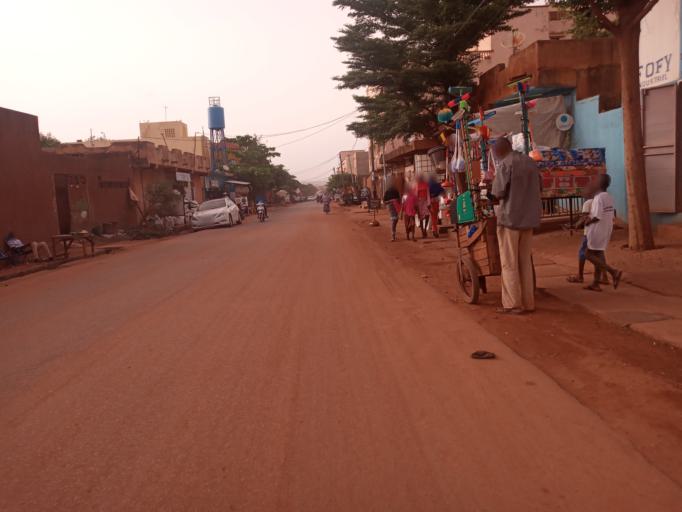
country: ML
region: Bamako
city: Bamako
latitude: 12.5559
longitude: -7.9903
